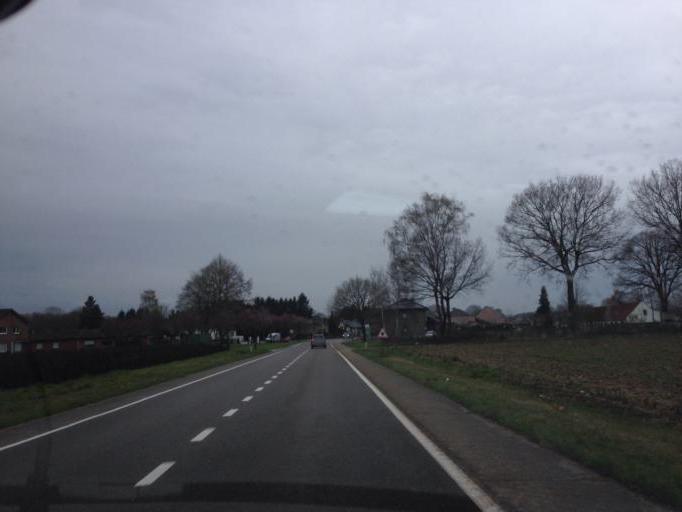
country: BE
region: Flanders
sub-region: Provincie Limburg
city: Opglabbeek
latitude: 51.0684
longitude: 5.5327
